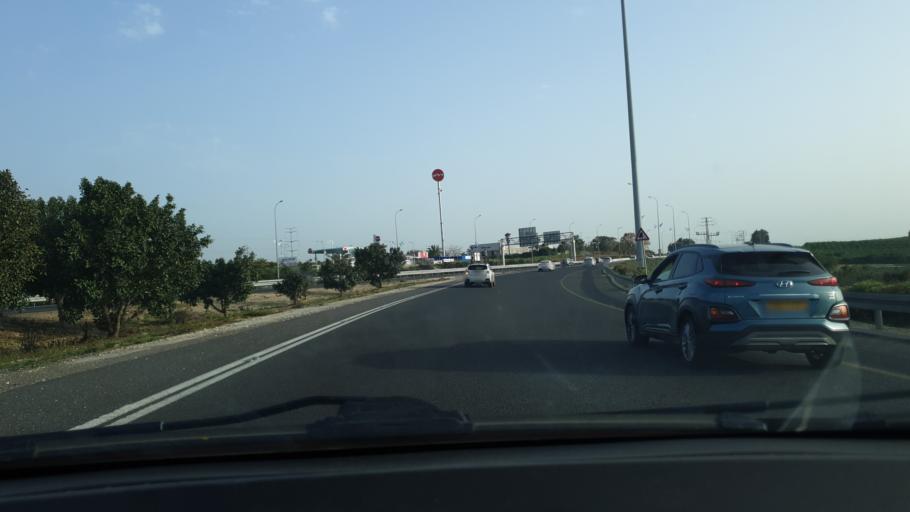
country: IL
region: Central District
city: Even Yehuda
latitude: 32.2529
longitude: 34.8898
